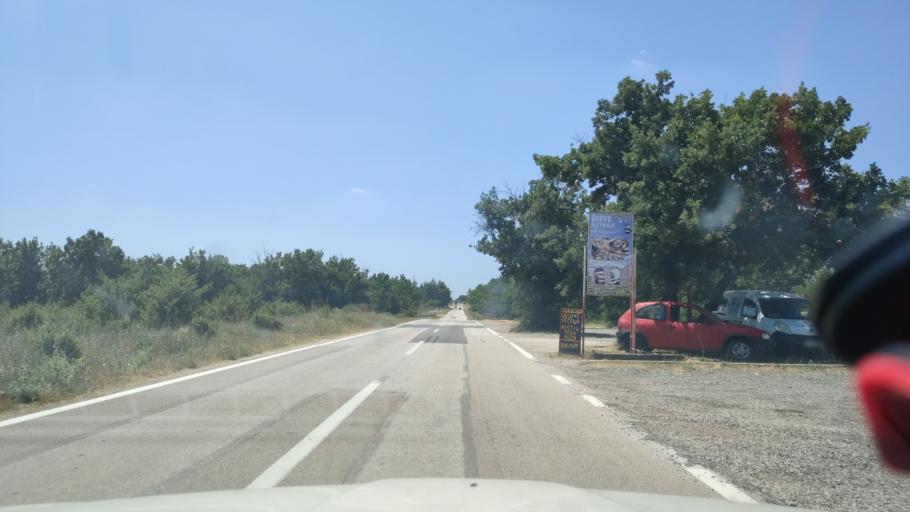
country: HR
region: Sibensko-Kniniska
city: Kistanje
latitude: 43.9904
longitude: 15.9778
